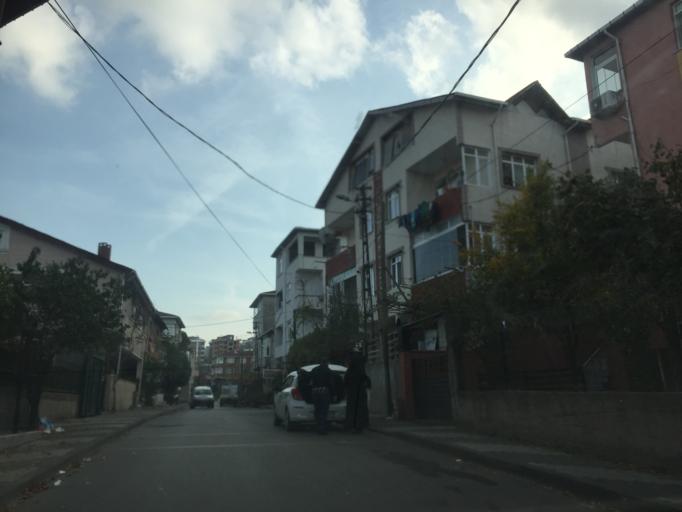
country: TR
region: Istanbul
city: Sultanbeyli
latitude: 40.9448
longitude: 29.2976
